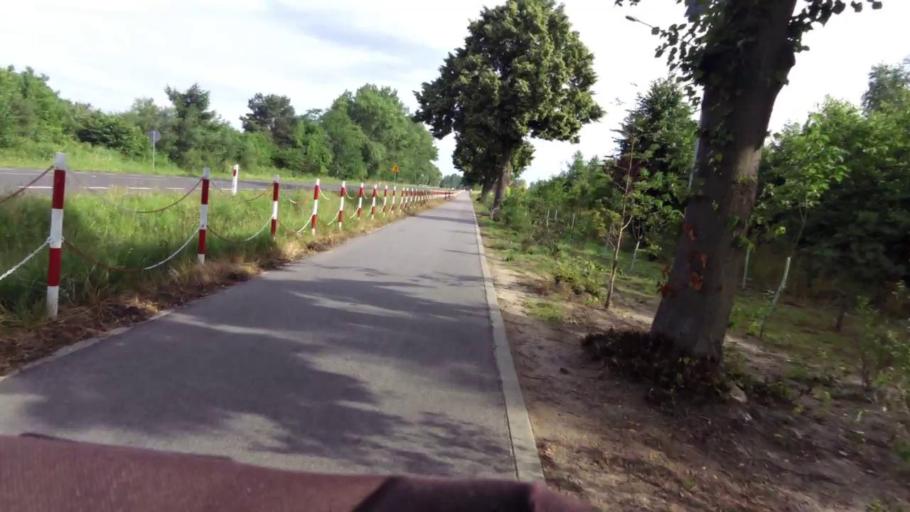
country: PL
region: West Pomeranian Voivodeship
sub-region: Powiat kamienski
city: Dziwnow
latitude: 54.0219
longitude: 14.8098
